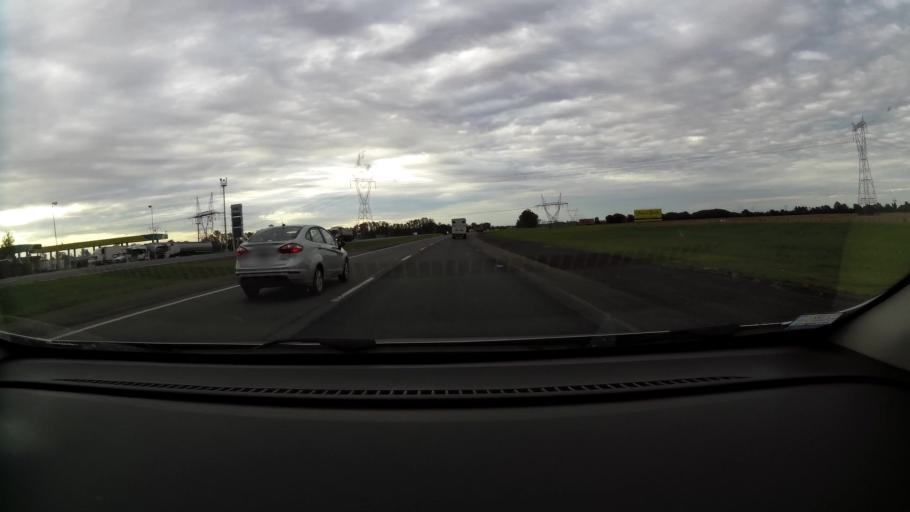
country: AR
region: Buenos Aires
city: San Nicolas de los Arroyos
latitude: -33.4303
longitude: -60.1753
